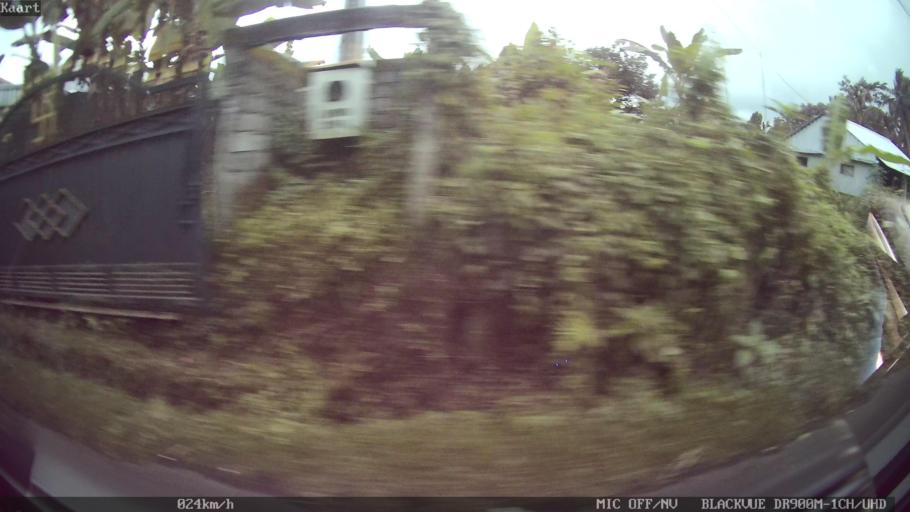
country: ID
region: Bali
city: Peneng
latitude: -8.3705
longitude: 115.1783
